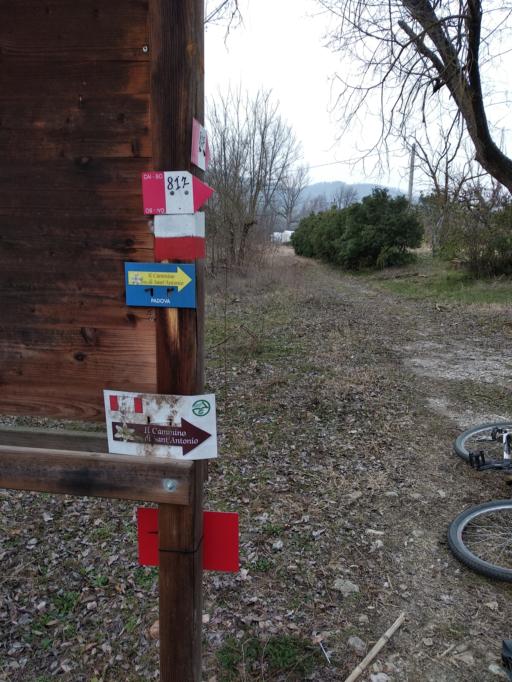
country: IT
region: Emilia-Romagna
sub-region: Provincia di Bologna
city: Pulce
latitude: 44.4150
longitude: 11.4257
